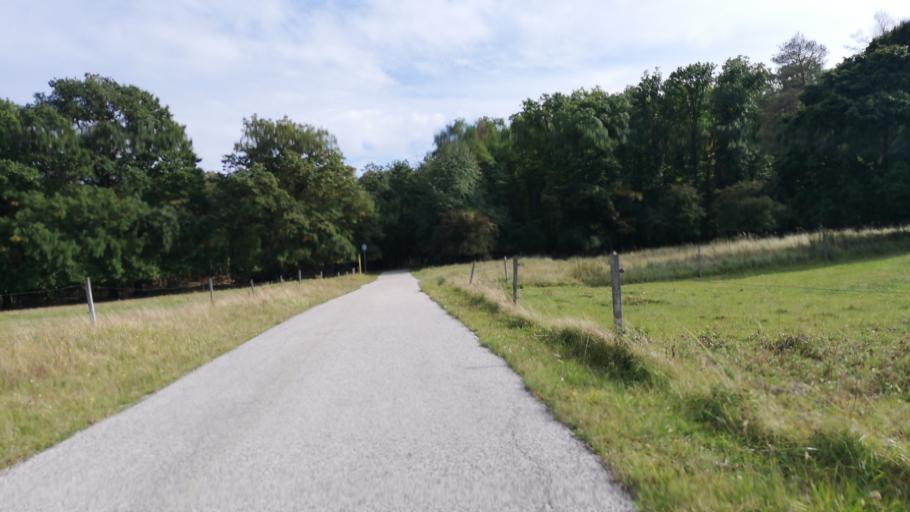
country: CZ
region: South Moravian
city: Petrov
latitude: 48.8326
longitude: 17.3062
